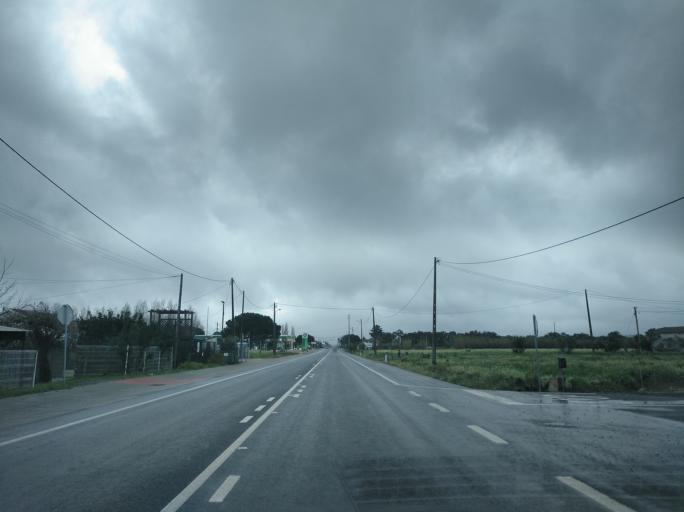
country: PT
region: Setubal
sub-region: Grandola
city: Grandola
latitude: 38.2184
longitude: -8.5579
